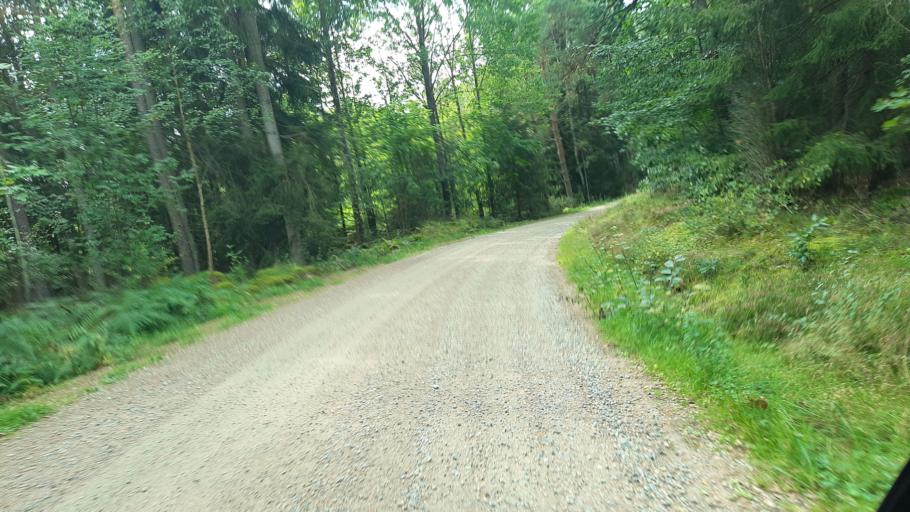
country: SE
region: Blekinge
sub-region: Ronneby Kommun
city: Brakne-Hoby
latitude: 56.4196
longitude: 15.1842
